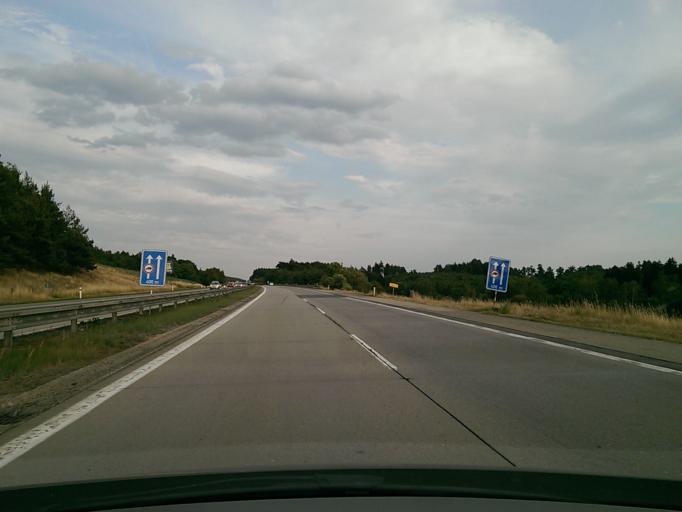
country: CZ
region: Vysocina
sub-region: Okres Zd'ar nad Sazavou
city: Velke Mezirici
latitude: 49.3373
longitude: 16.0582
